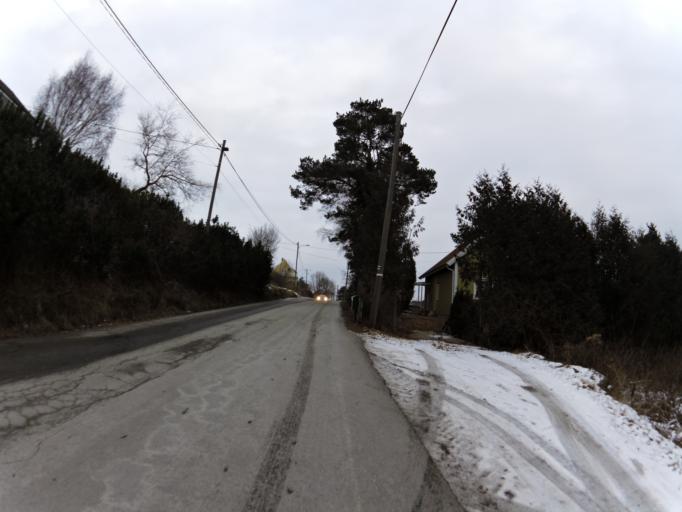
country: NO
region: Ostfold
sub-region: Fredrikstad
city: Fredrikstad
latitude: 59.2121
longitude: 10.8889
